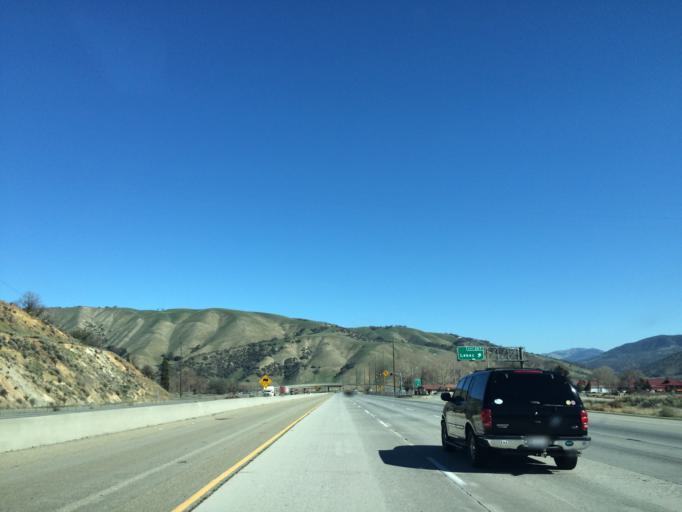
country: US
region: California
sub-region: Kern County
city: Lebec
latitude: 34.8309
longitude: -118.8681
